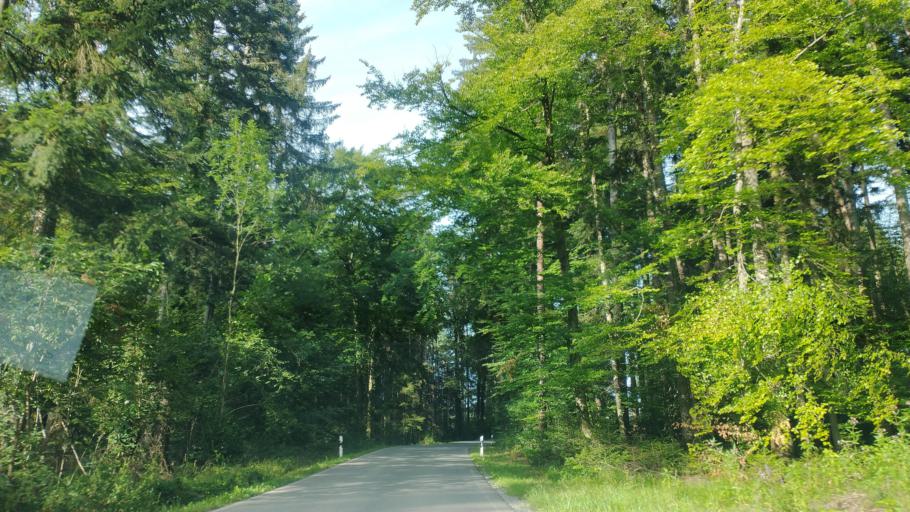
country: DE
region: Baden-Wuerttemberg
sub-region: Tuebingen Region
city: Neukirch
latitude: 47.6554
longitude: 9.6501
